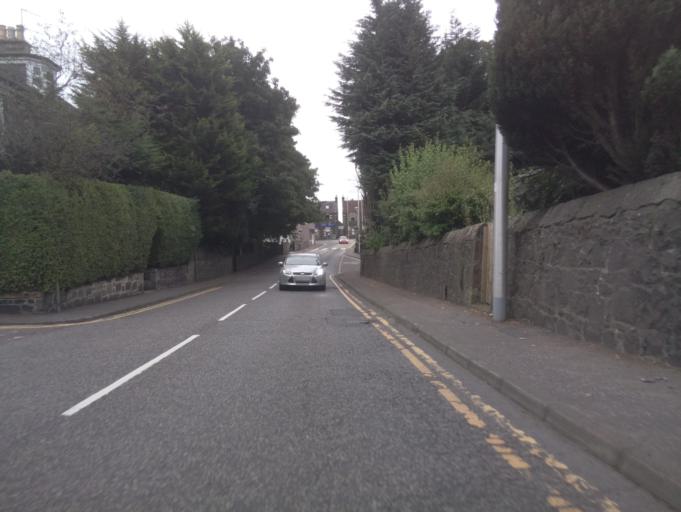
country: GB
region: Scotland
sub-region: Fife
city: Leslie
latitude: 56.2014
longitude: -3.2171
